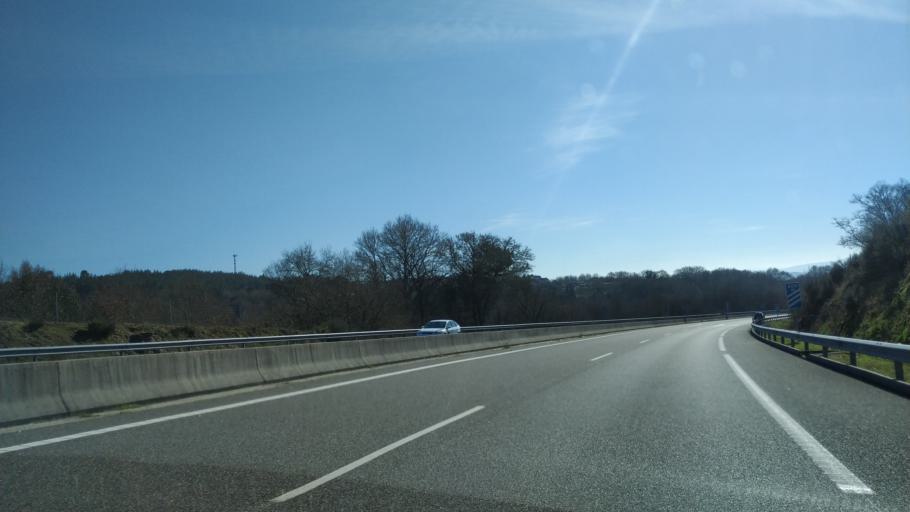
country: ES
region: Galicia
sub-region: Provincia de Ourense
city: Maside
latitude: 42.4125
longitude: -8.0131
